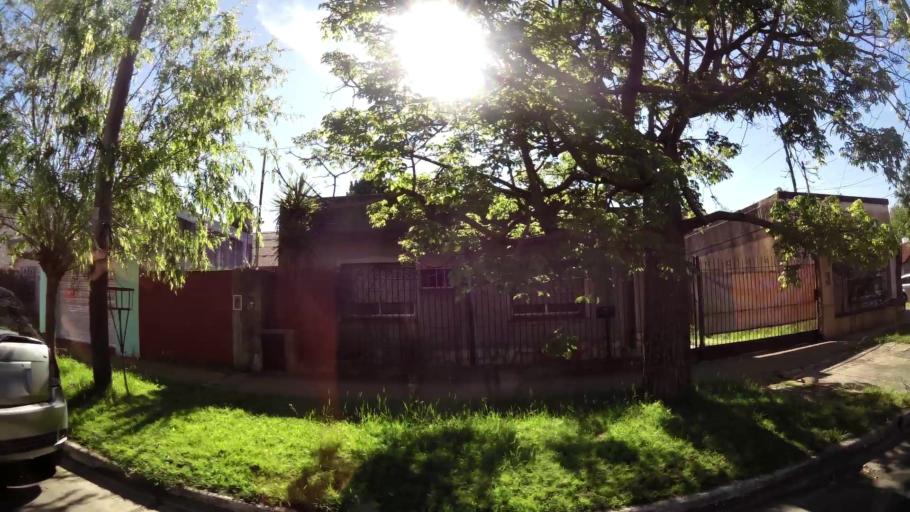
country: AR
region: Buenos Aires
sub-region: Partido de Lomas de Zamora
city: Lomas de Zamora
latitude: -34.7643
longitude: -58.4200
